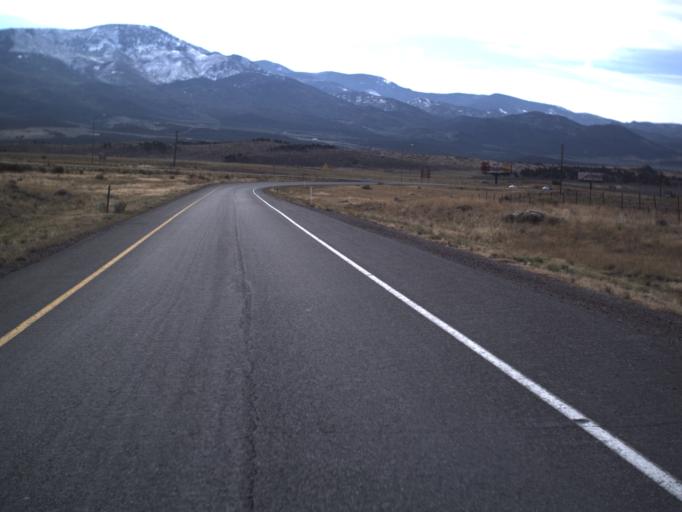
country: US
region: Utah
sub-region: Beaver County
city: Beaver
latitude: 38.6153
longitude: -112.6114
